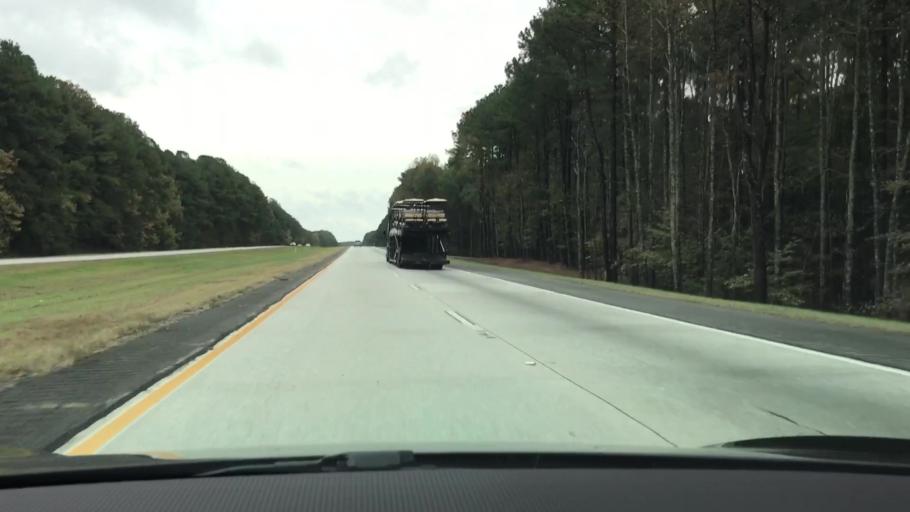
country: US
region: Georgia
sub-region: Taliaferro County
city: Crawfordville
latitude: 33.5076
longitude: -82.8378
